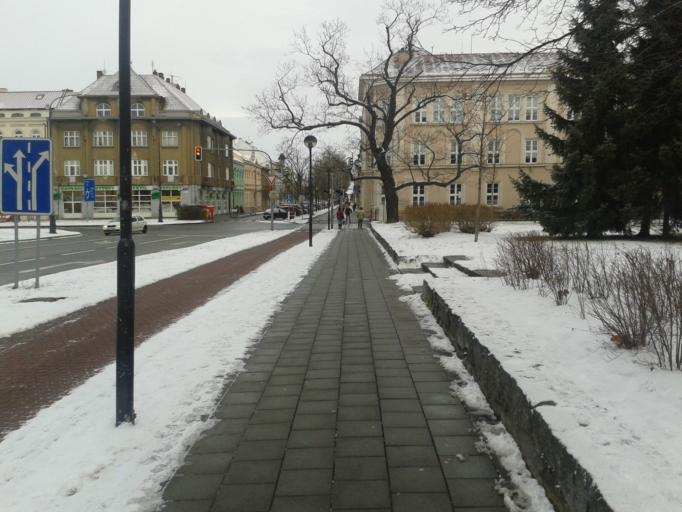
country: CZ
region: Olomoucky
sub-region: Okres Prostejov
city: Prostejov
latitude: 49.4738
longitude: 17.1097
